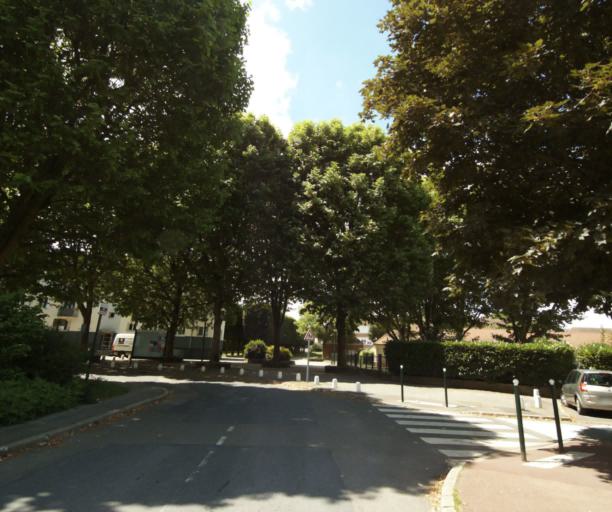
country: FR
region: Ile-de-France
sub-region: Departement des Yvelines
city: Fontenay-le-Fleury
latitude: 48.8064
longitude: 2.0567
